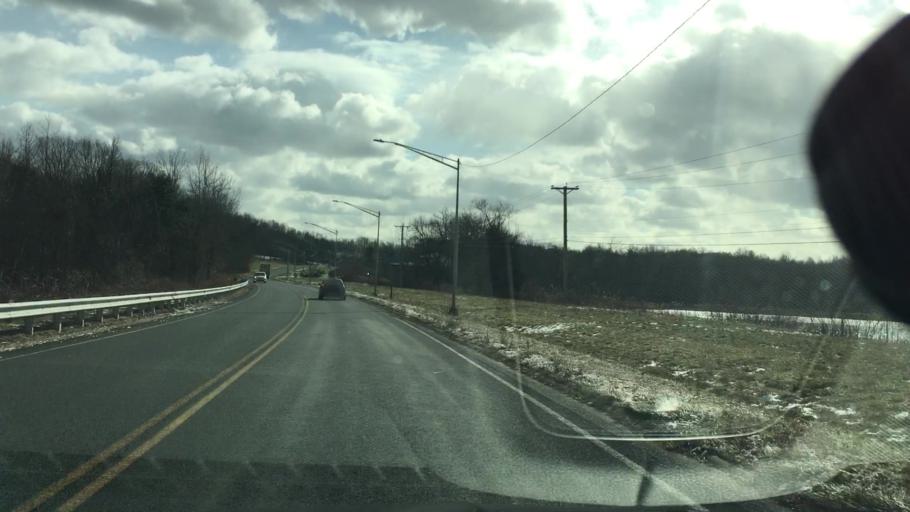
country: US
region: Connecticut
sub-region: New Haven County
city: Meriden
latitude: 41.5062
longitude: -72.7666
